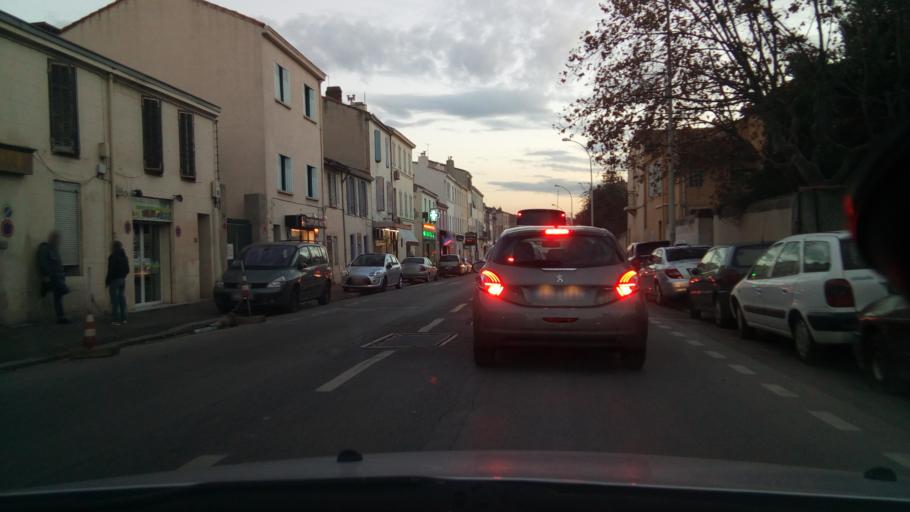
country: FR
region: Provence-Alpes-Cote d'Azur
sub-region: Departement des Bouches-du-Rhone
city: Marseille 14
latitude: 43.3246
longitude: 5.3671
